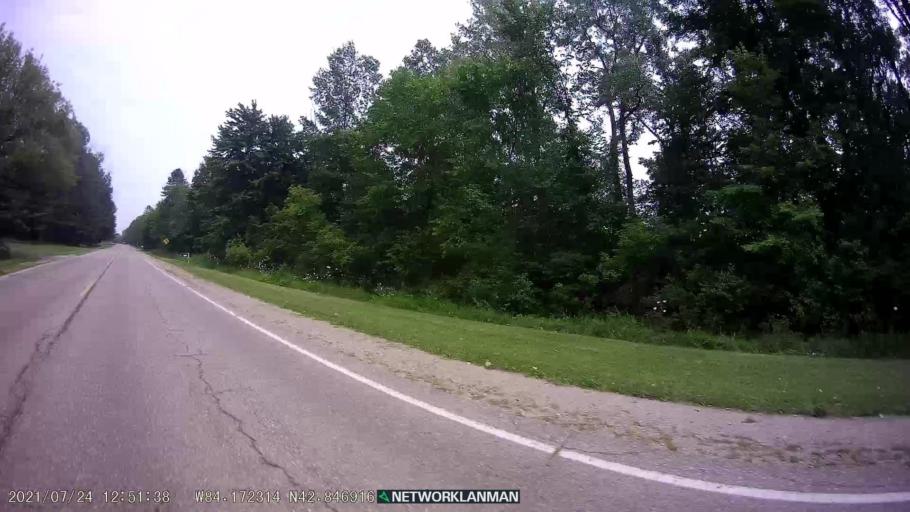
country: US
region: Michigan
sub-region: Shiawassee County
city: Perry
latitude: 42.8471
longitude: -84.1711
